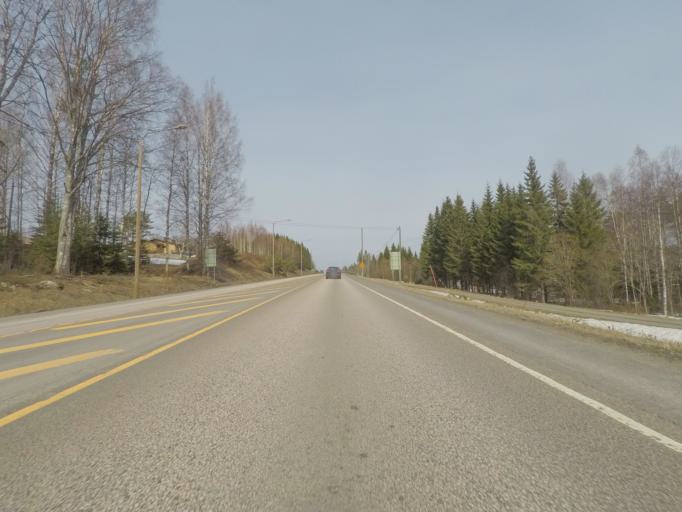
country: FI
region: Central Finland
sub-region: Jyvaeskylae
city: Toivakka
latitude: 62.0297
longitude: 26.0481
